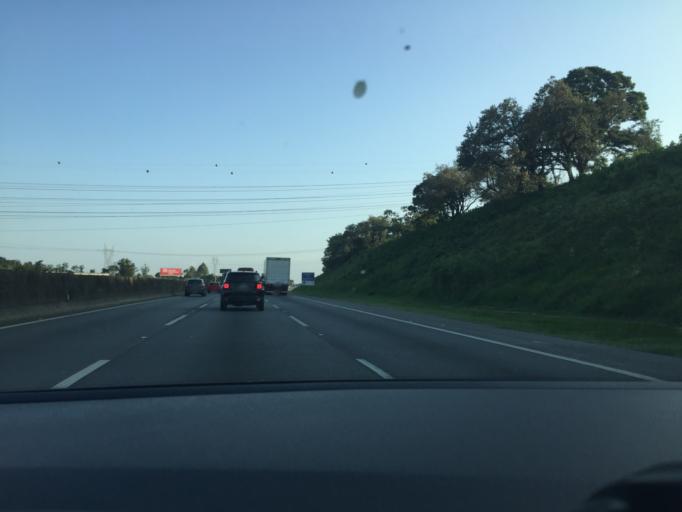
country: BR
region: Sao Paulo
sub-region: Louveira
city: Louveira
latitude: -23.1148
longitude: -46.9570
